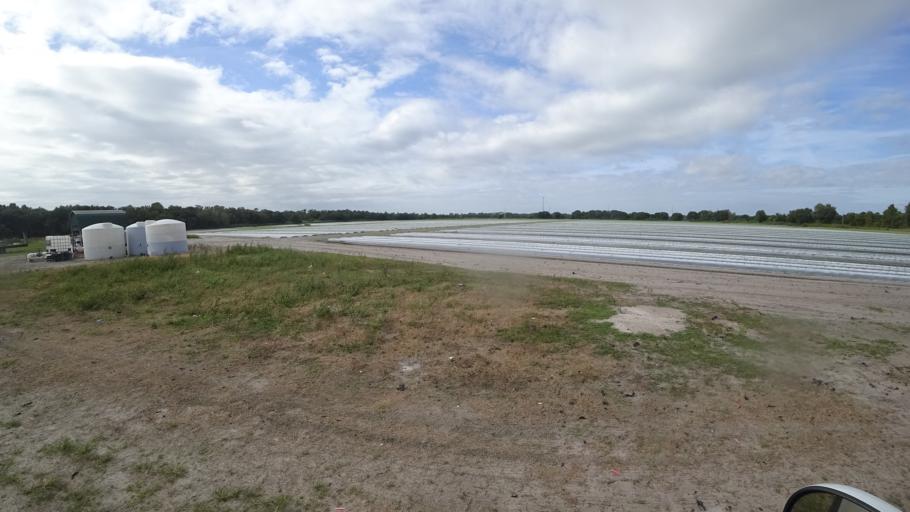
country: US
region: Florida
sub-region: Hillsborough County
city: Wimauma
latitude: 27.5993
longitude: -82.3251
